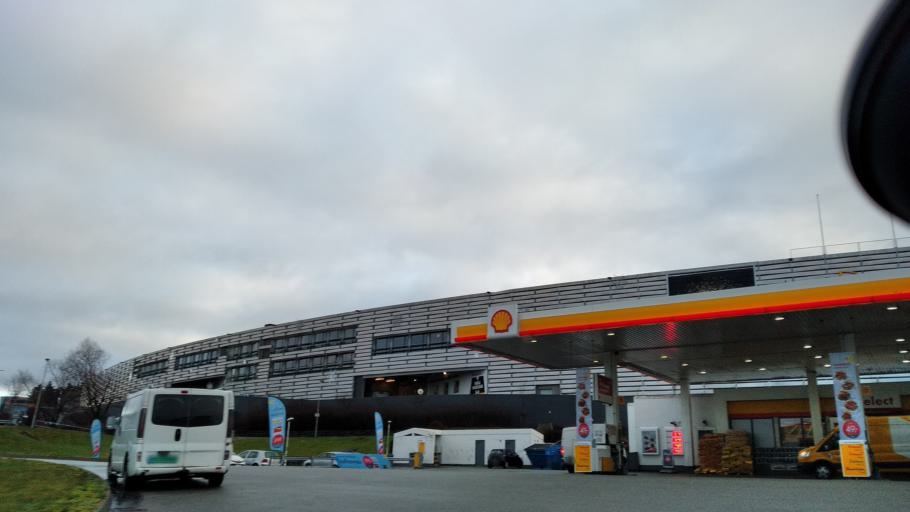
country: NO
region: Rogaland
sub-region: Stavanger
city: Stavanger
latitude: 58.9528
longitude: 5.6762
